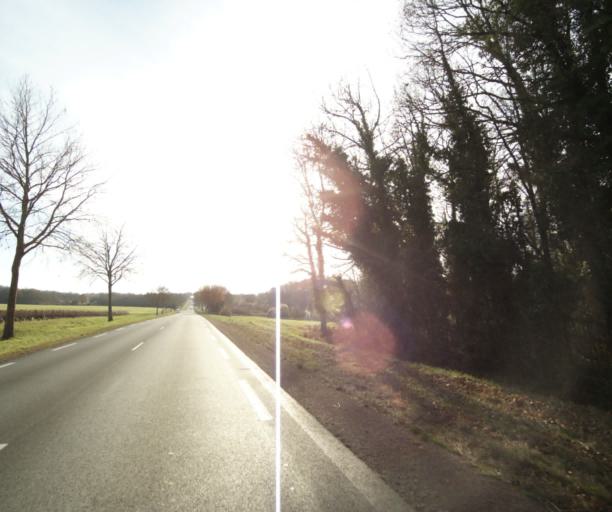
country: FR
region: Poitou-Charentes
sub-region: Departement de la Charente-Maritime
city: Saint-Hilaire-de-Villefranche
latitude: 45.8295
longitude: -0.5406
